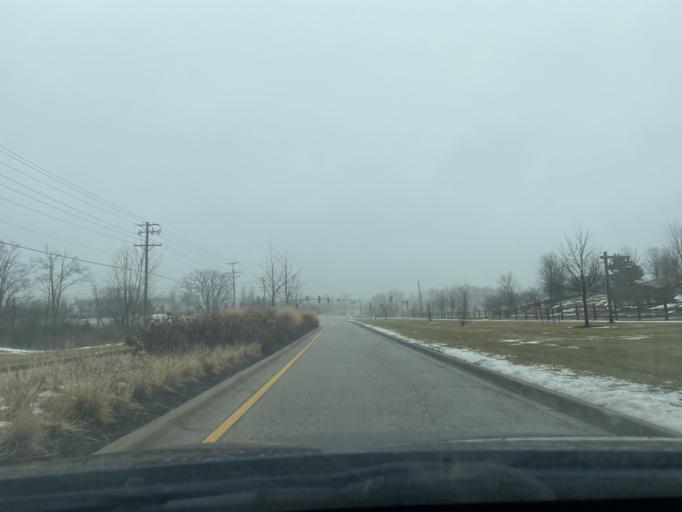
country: US
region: Illinois
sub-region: Lake County
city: Volo
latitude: 42.3225
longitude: -88.1451
